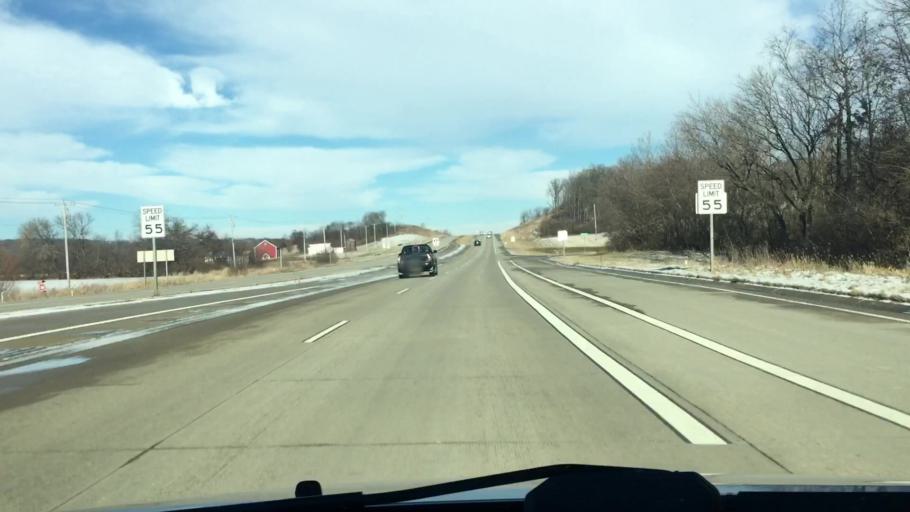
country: US
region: Wisconsin
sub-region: Waukesha County
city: Mukwonago
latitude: 42.9028
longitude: -88.3453
